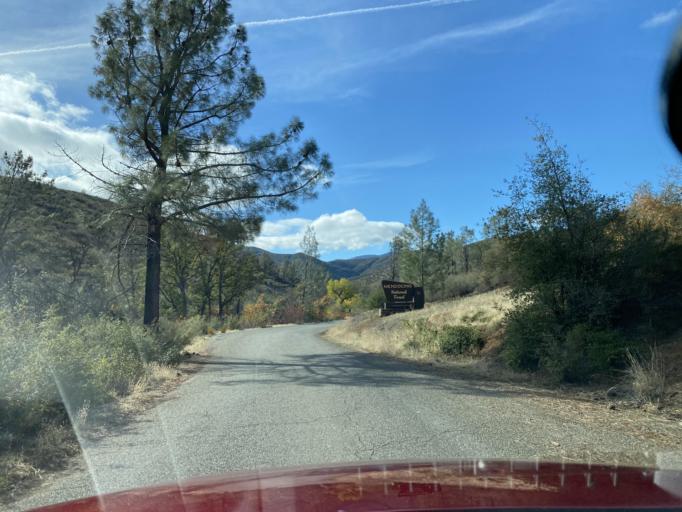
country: US
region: California
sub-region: Lake County
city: Lucerne
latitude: 39.3672
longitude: -122.6179
